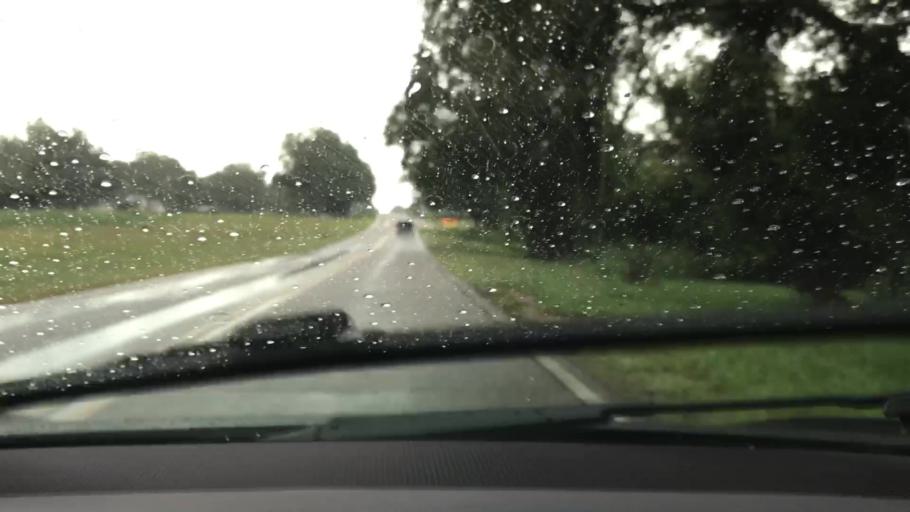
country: US
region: Alabama
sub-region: Covington County
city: Opp
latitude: 31.2155
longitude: -86.1704
